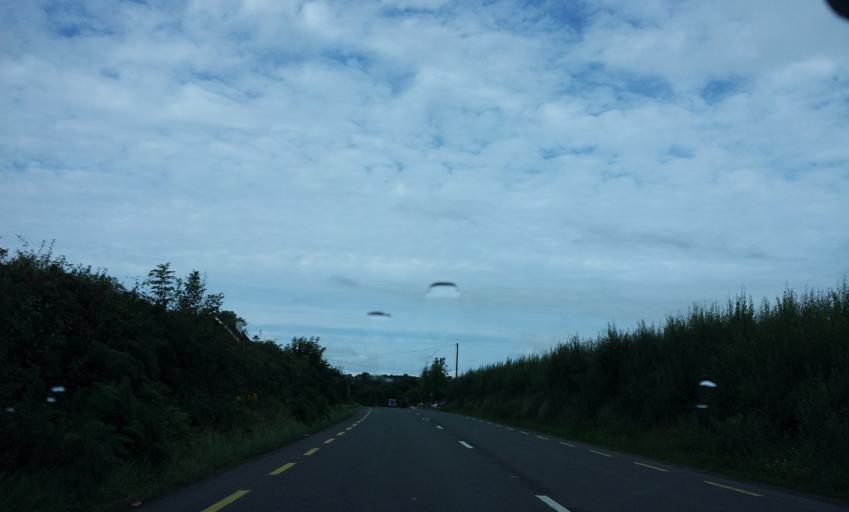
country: IE
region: Munster
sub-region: Ciarrai
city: Cill Airne
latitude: 52.0740
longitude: -9.6180
